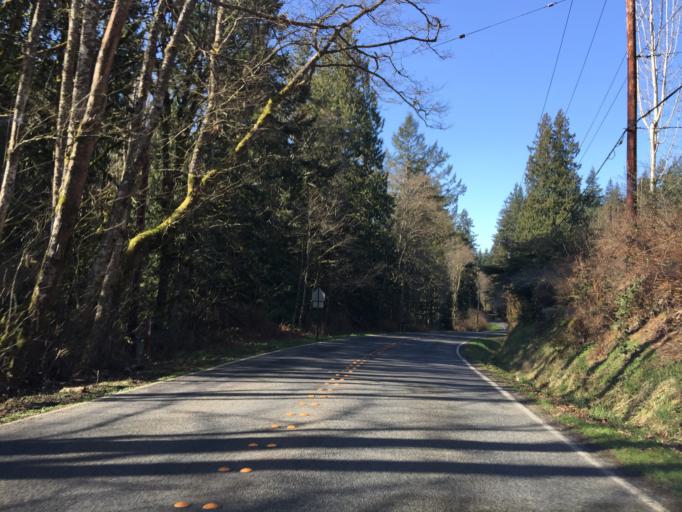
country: US
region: Washington
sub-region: Whatcom County
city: Bellingham
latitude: 48.7022
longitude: -122.4779
